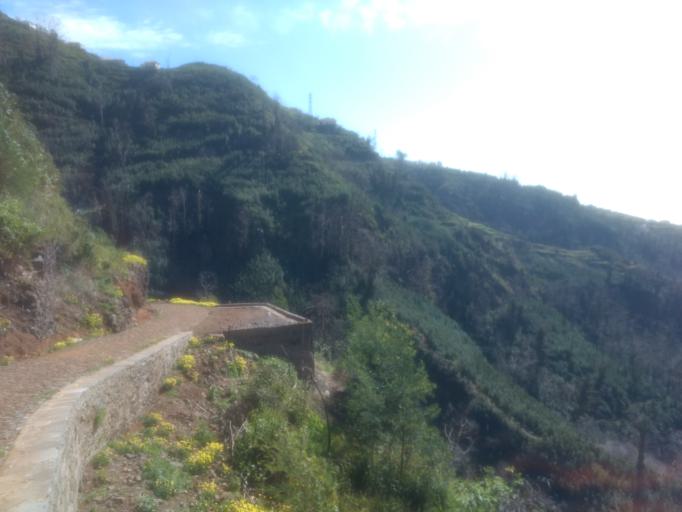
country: PT
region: Madeira
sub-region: Funchal
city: Nossa Senhora do Monte
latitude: 32.6779
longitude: -16.8968
